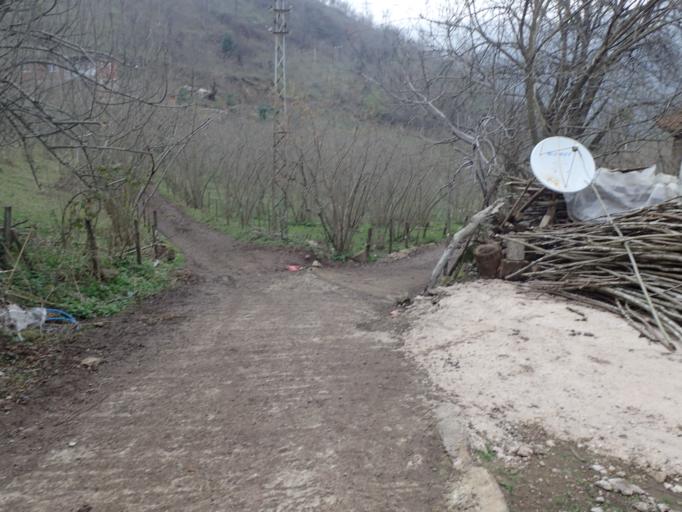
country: TR
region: Ordu
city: Camas
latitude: 40.9233
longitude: 37.5644
